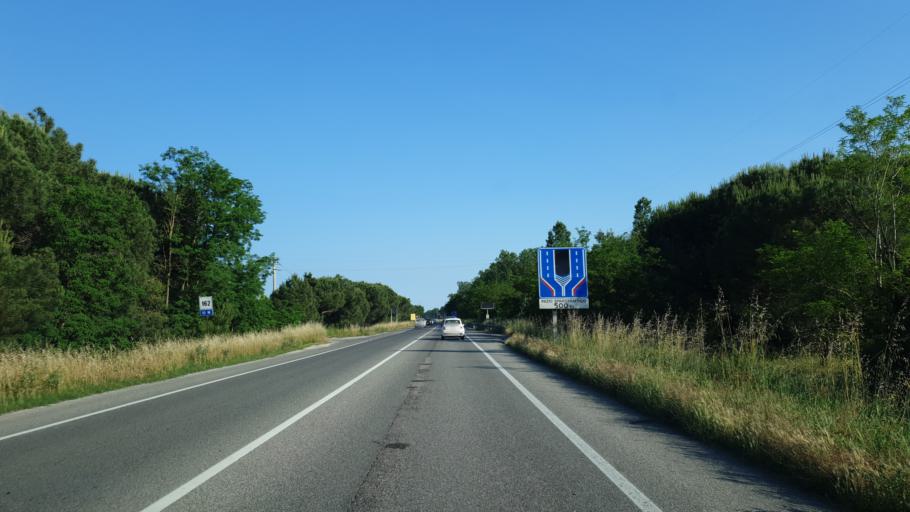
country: IT
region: Emilia-Romagna
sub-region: Provincia di Ravenna
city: Fosso Ghiaia
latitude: 44.3409
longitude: 12.2664
